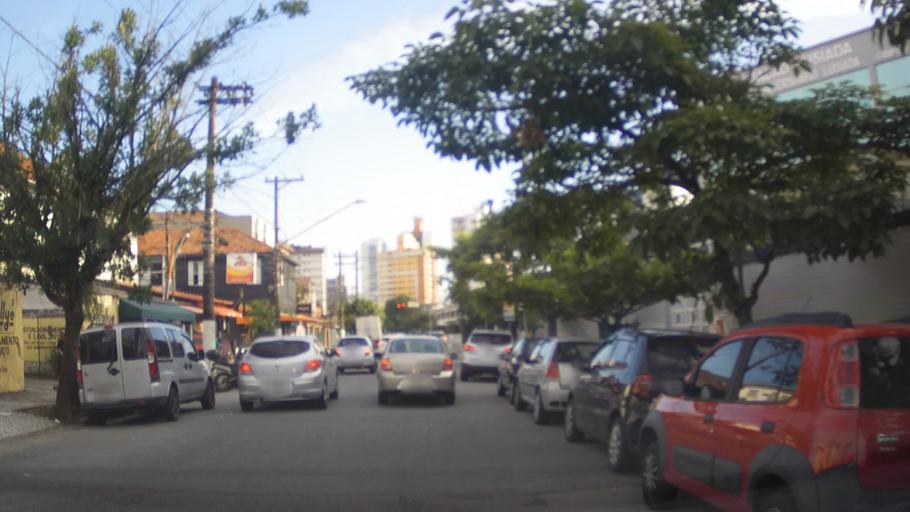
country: BR
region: Sao Paulo
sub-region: Santos
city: Santos
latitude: -23.9620
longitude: -46.3216
